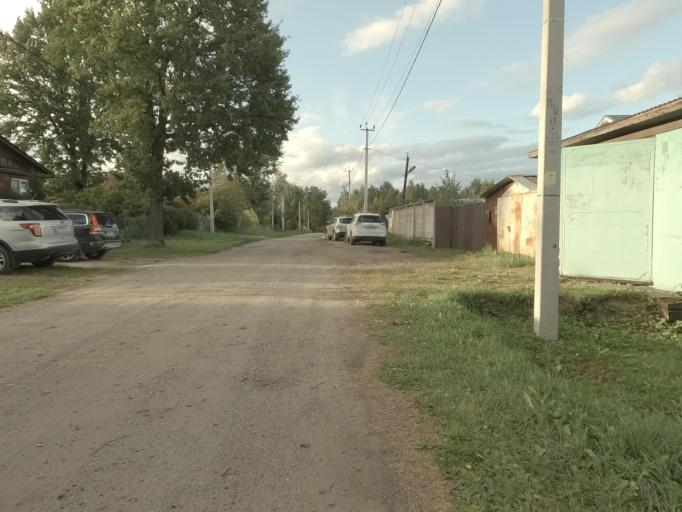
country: RU
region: Leningrad
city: Mga
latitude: 59.7614
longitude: 31.0717
